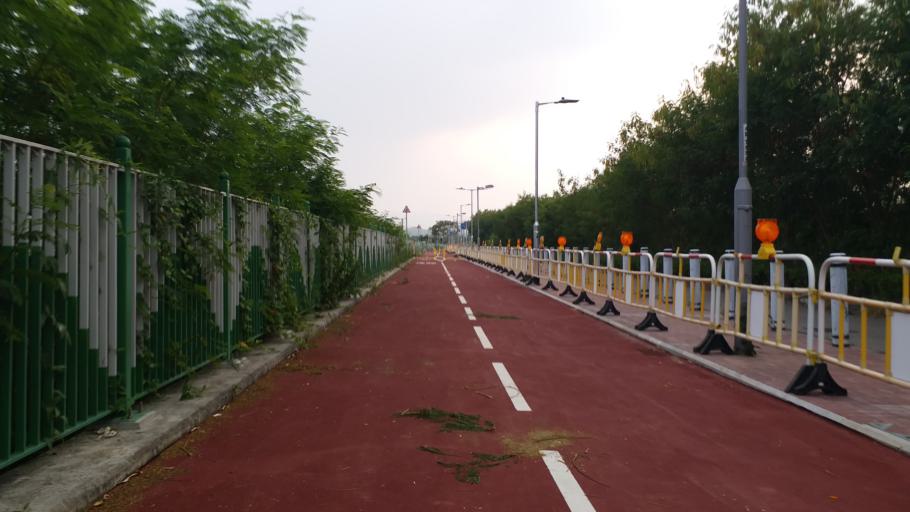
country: HK
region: Yuen Long
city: Yuen Long Kau Hui
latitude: 22.4680
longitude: 114.0477
